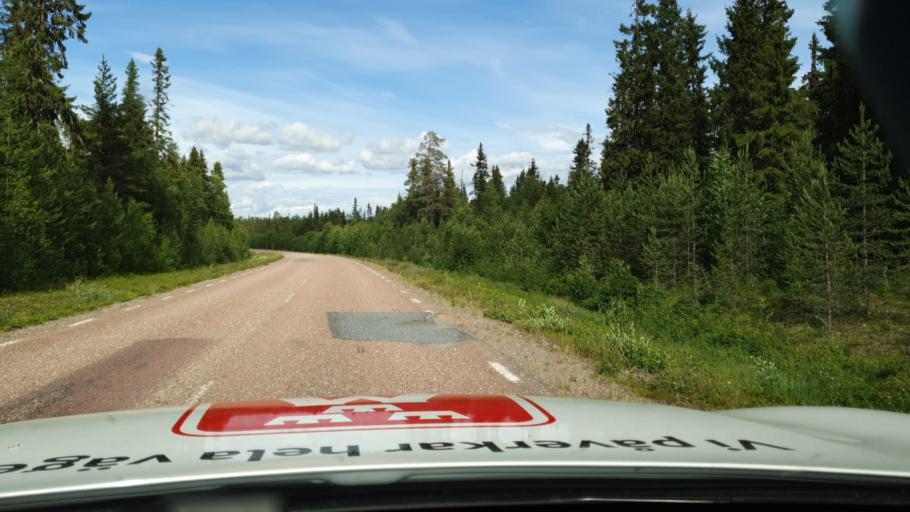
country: SE
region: Dalarna
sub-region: Alvdalens Kommun
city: AElvdalen
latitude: 61.7664
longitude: 13.4760
